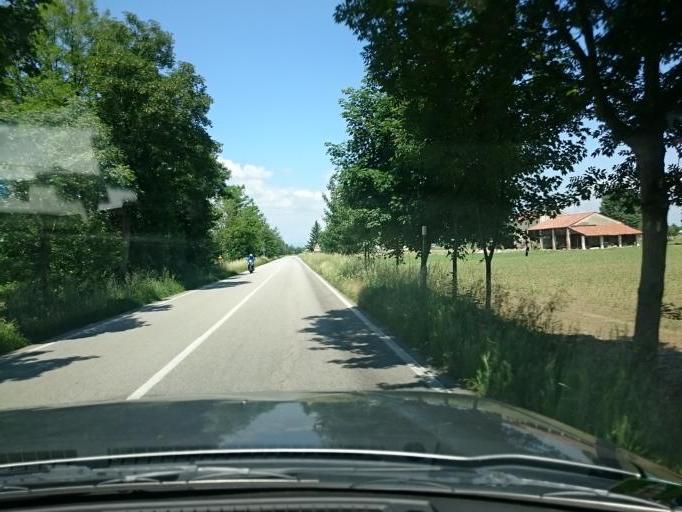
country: IT
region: Veneto
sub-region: Provincia di Vicenza
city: Montegalda
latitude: 45.4542
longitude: 11.6555
